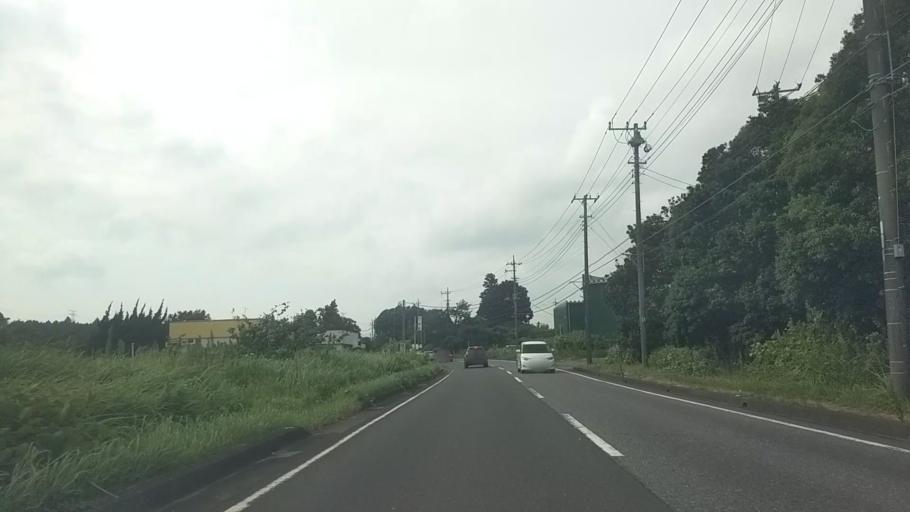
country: JP
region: Chiba
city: Kimitsu
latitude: 35.2760
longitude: 139.9938
